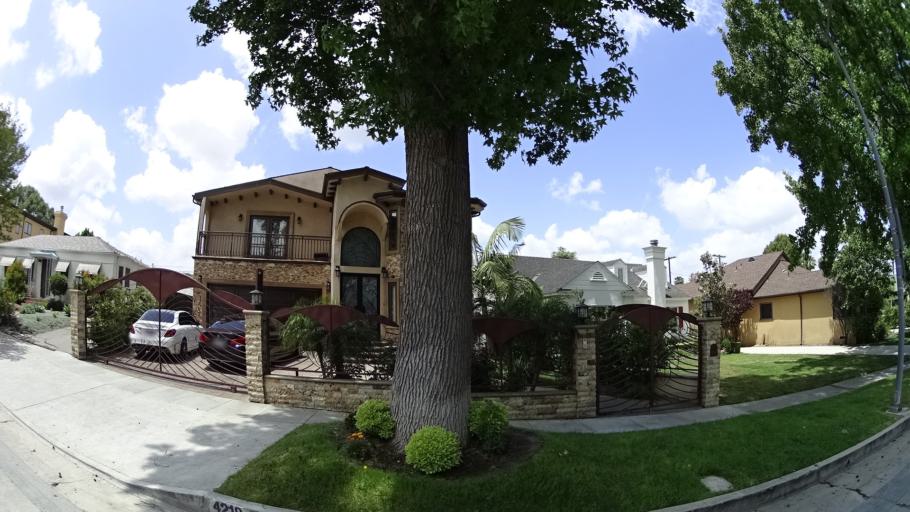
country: US
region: California
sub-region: Los Angeles County
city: Sherman Oaks
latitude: 34.1472
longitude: -118.4317
